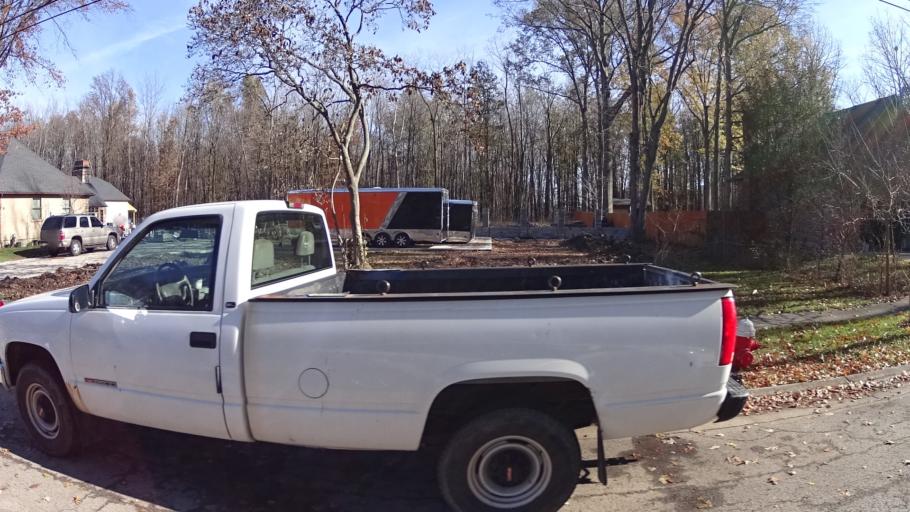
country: US
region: Ohio
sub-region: Lorain County
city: Sheffield Lake
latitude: 41.4913
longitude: -82.0726
